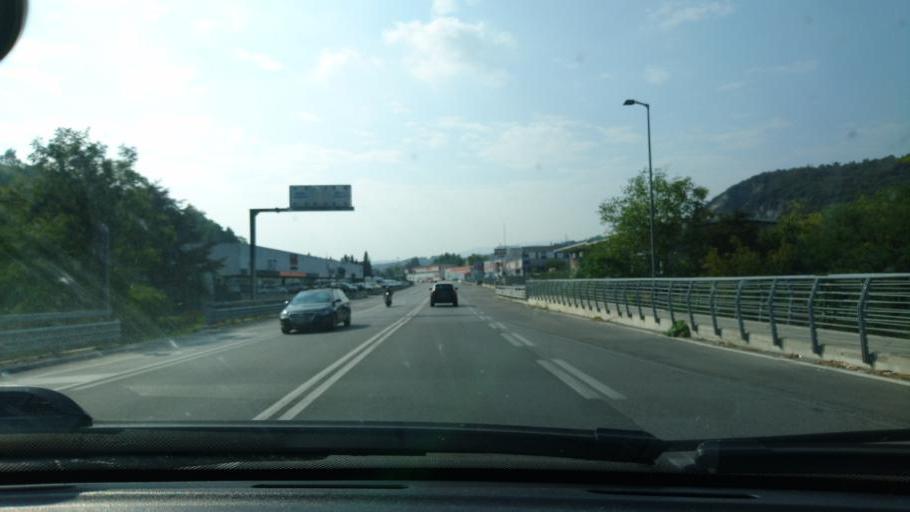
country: IT
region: Liguria
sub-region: Provincia di Savona
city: Cairo Montenotte
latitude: 44.3925
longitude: 8.2817
